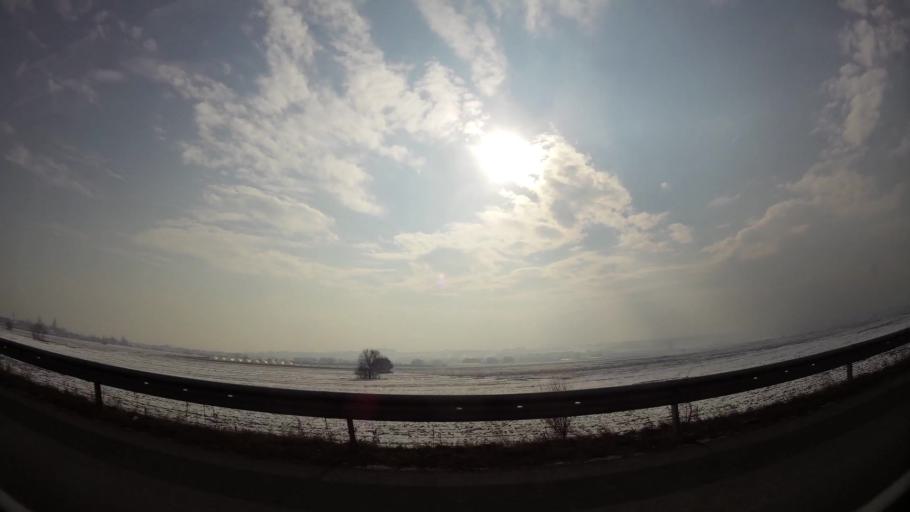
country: MK
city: Creshevo
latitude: 42.0311
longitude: 21.5041
